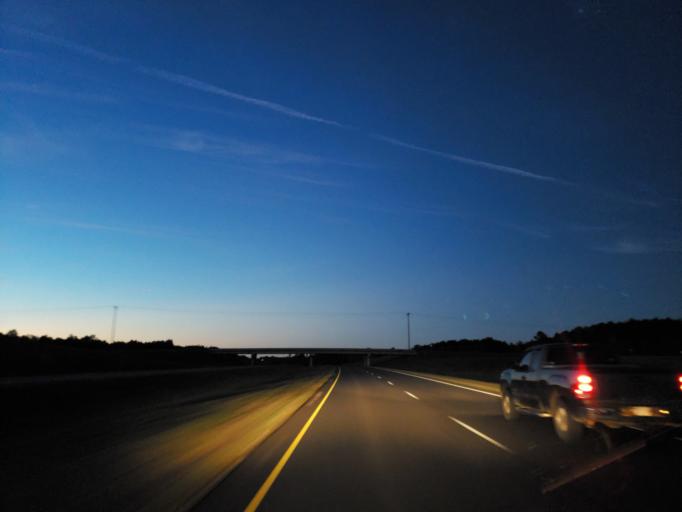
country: US
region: Mississippi
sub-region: Clarke County
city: Quitman
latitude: 32.0572
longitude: -88.6775
